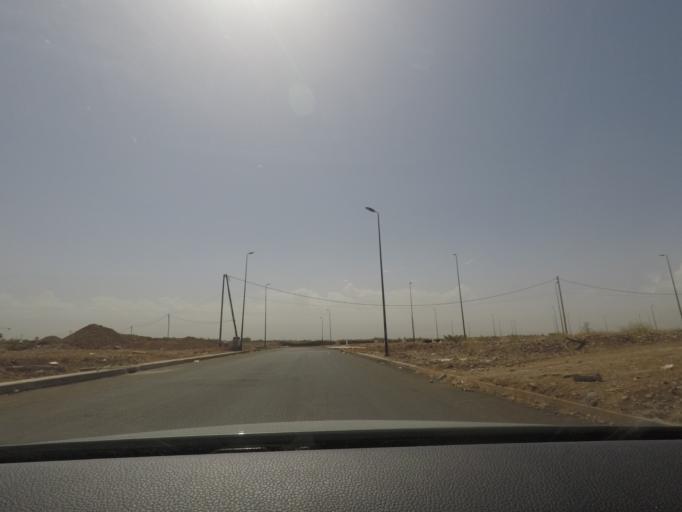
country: MA
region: Marrakech-Tensift-Al Haouz
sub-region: Marrakech
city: Marrakesh
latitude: 31.5840
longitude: -8.0376
